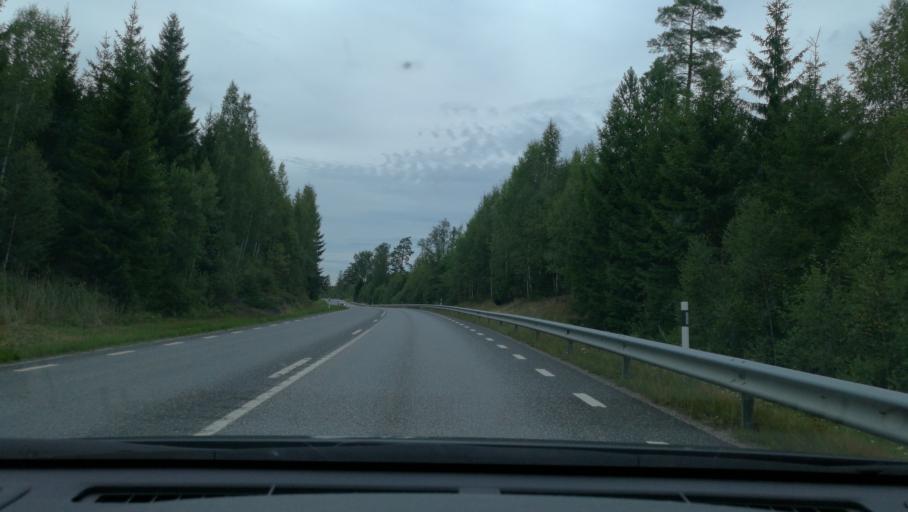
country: SE
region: Soedermanland
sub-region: Katrineholms Kommun
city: Katrineholm
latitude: 58.9450
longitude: 16.1946
